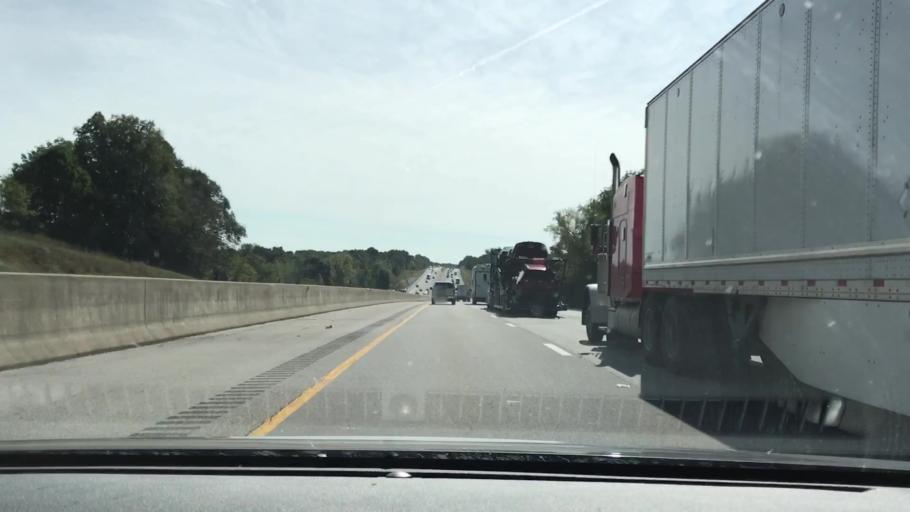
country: US
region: Kentucky
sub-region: Simpson County
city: Franklin
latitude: 36.7747
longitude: -86.4810
